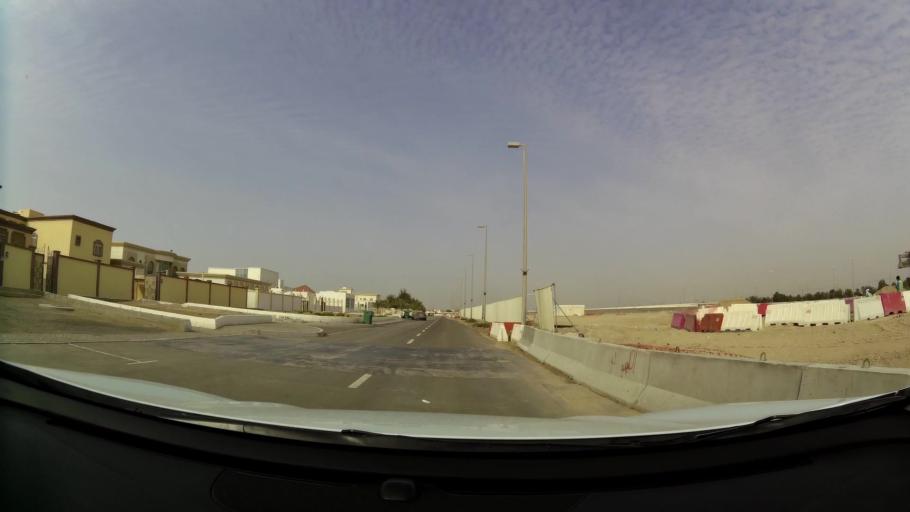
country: AE
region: Abu Dhabi
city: Abu Dhabi
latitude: 24.6181
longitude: 54.7119
